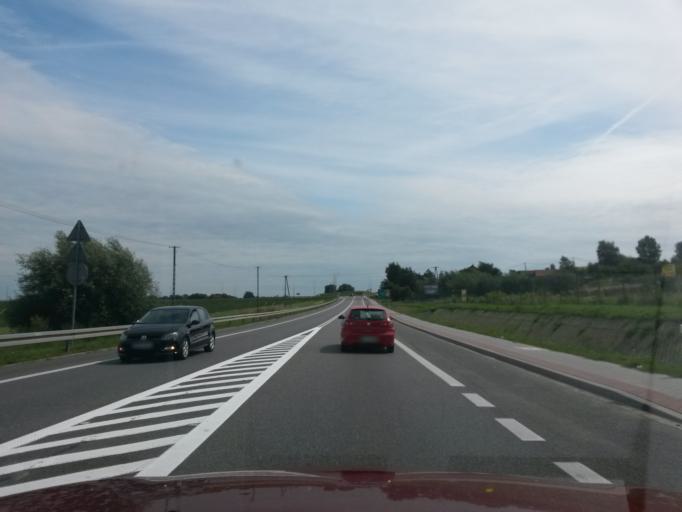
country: PL
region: Lesser Poland Voivodeship
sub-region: Powiat brzeski
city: Jasien
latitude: 49.9728
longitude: 20.5768
